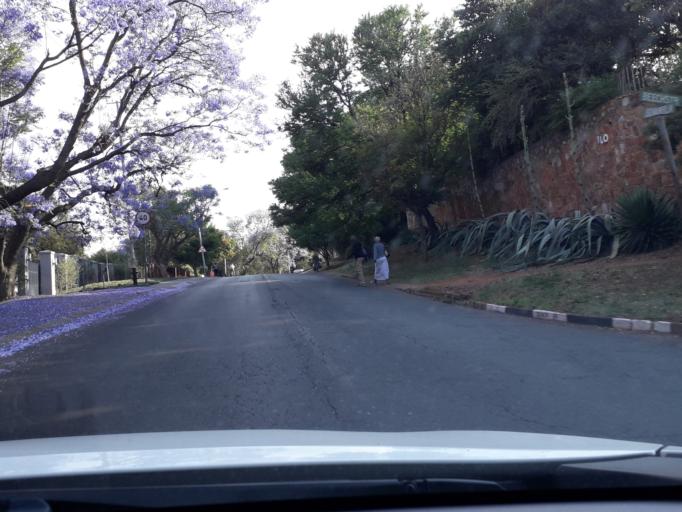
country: ZA
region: Gauteng
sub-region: City of Johannesburg Metropolitan Municipality
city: Roodepoort
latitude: -26.1473
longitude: 27.9577
